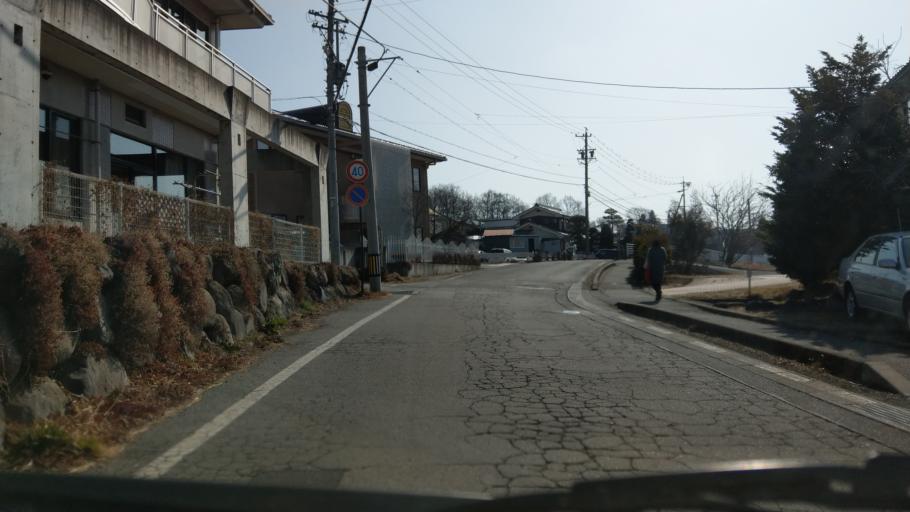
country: JP
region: Nagano
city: Ueda
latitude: 36.3689
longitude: 138.3571
